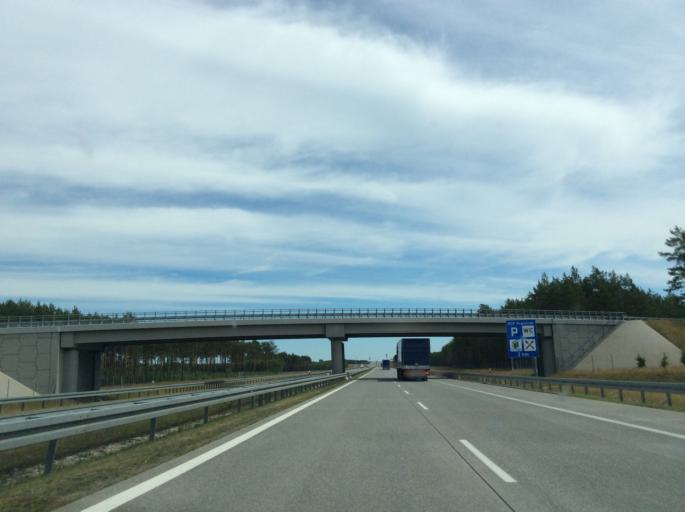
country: PL
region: Lubusz
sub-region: Powiat swiebodzinski
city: Szczaniec
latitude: 52.3022
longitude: 15.7470
